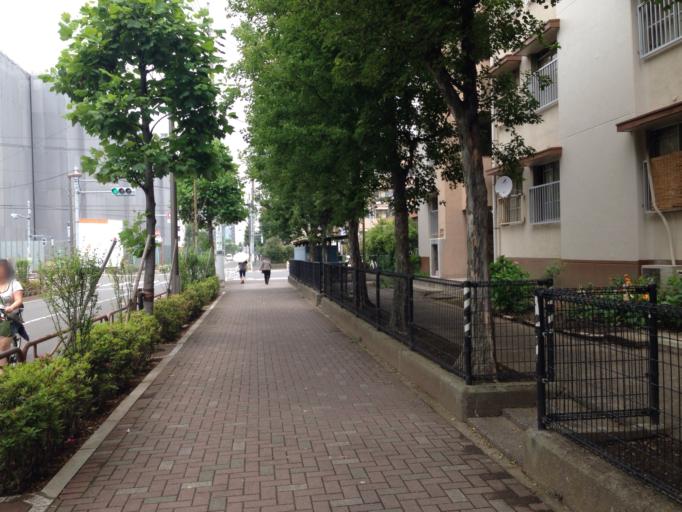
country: JP
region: Tokyo
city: Urayasu
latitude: 35.6485
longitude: 139.8092
